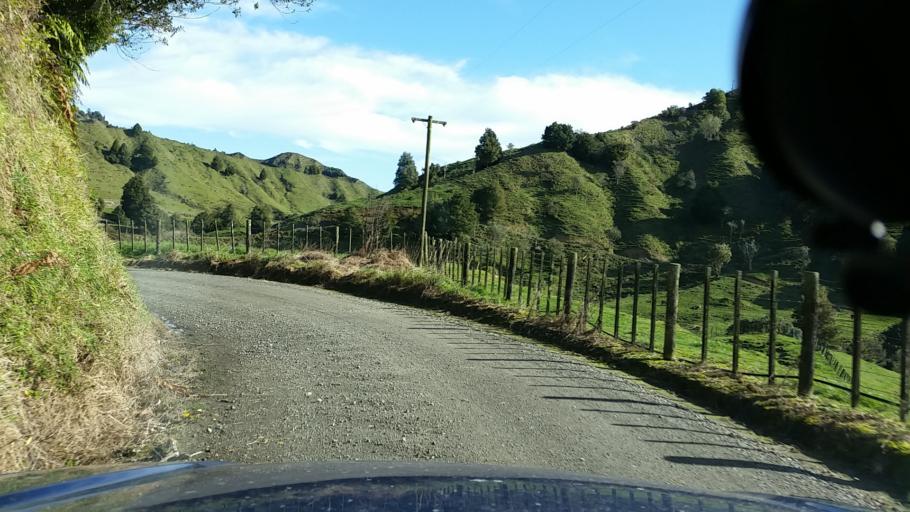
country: NZ
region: Taranaki
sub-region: New Plymouth District
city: Waitara
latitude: -39.0514
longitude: 174.7558
